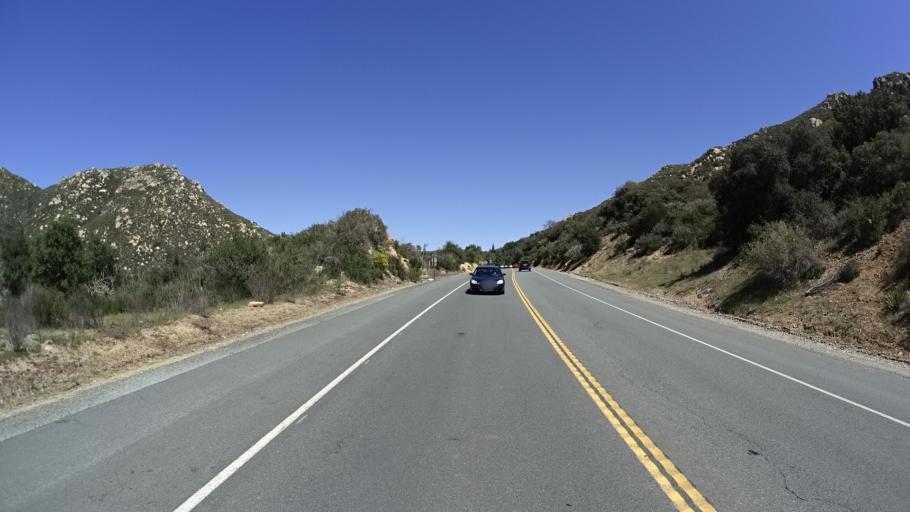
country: US
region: California
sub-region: San Diego County
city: Descanso
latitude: 32.8371
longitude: -116.6185
